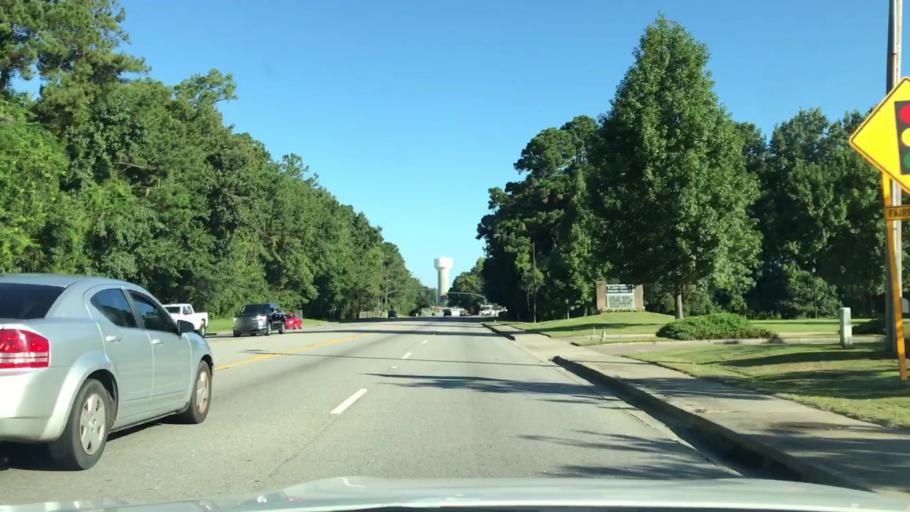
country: US
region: South Carolina
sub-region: Berkeley County
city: Goose Creek
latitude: 33.0286
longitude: -80.0576
